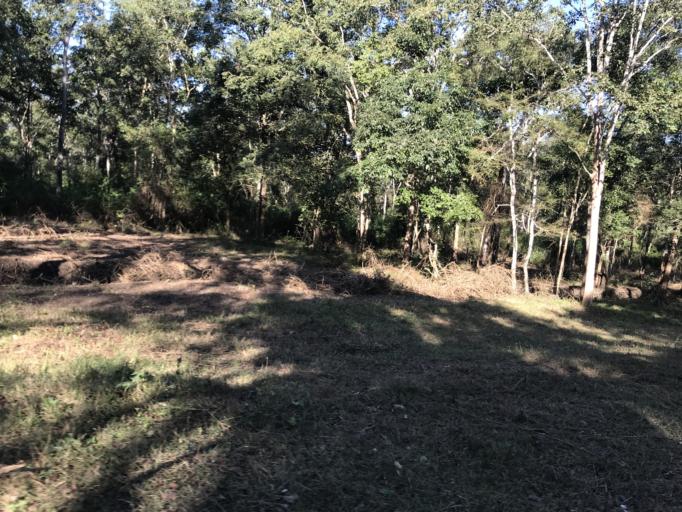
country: IN
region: Karnataka
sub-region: Mysore
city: Heggadadevankote
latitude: 11.9790
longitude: 76.2357
